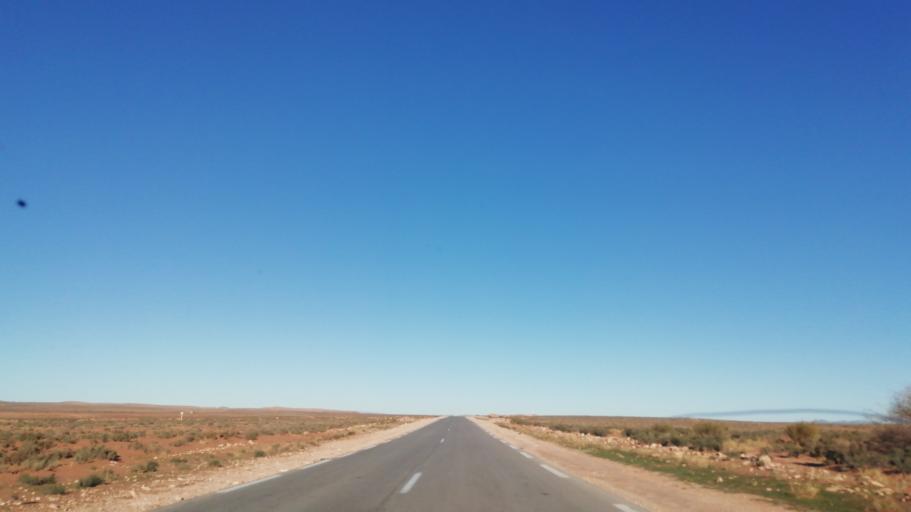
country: DZ
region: El Bayadh
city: El Abiodh Sidi Cheikh
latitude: 33.1171
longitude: 0.2685
